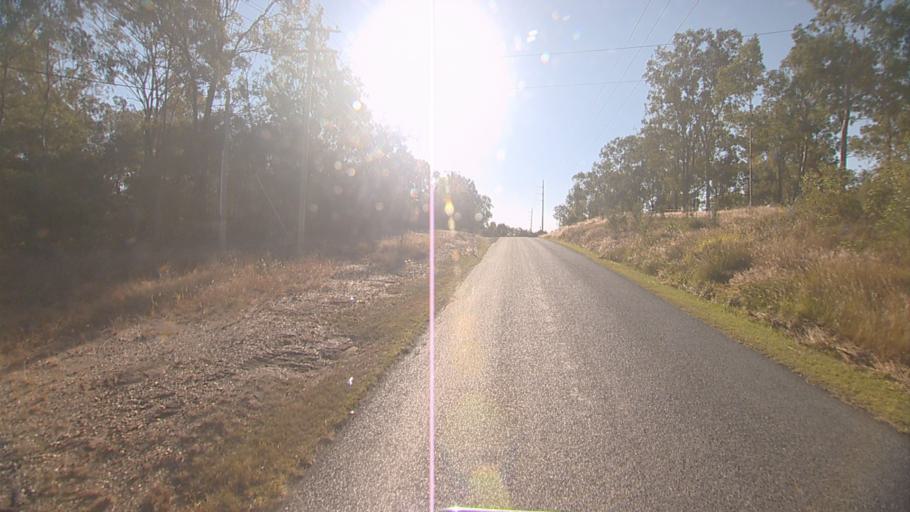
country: AU
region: Queensland
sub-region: Logan
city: North Maclean
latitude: -27.8066
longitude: 153.0425
